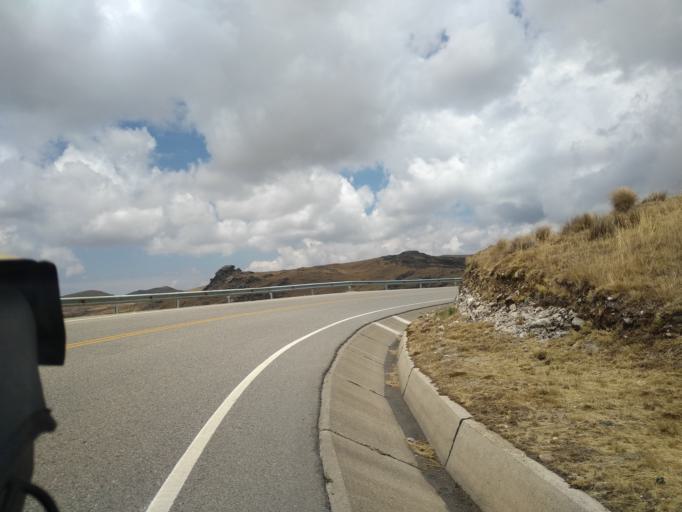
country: PE
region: La Libertad
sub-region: Provincia de Santiago de Chuco
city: Quiruvilca
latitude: -7.9413
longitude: -78.1857
